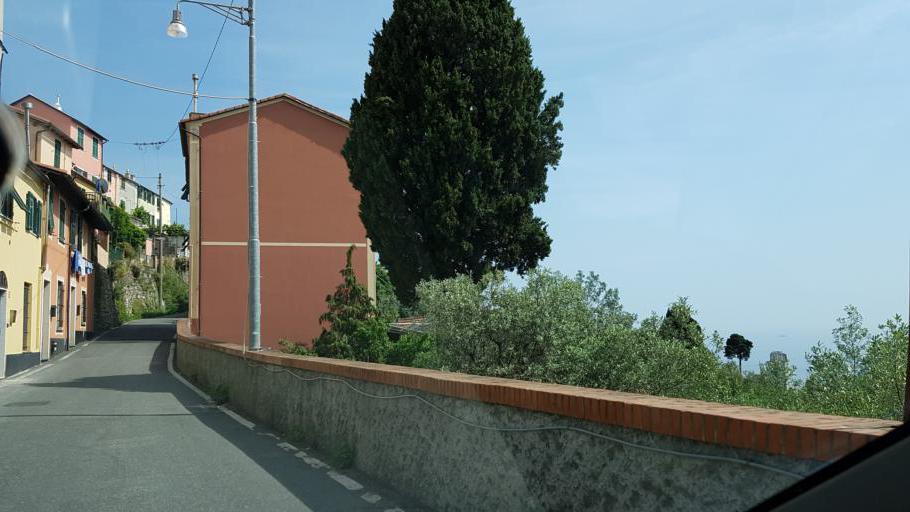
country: IT
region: Liguria
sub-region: Provincia di Genova
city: Bogliasco
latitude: 44.4055
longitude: 9.0005
